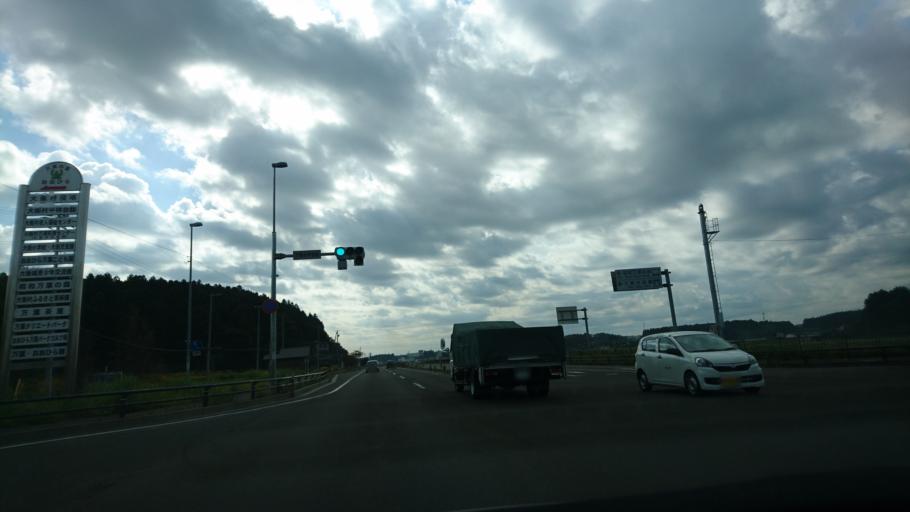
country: JP
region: Miyagi
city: Tomiya
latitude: 38.4658
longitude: 140.8768
